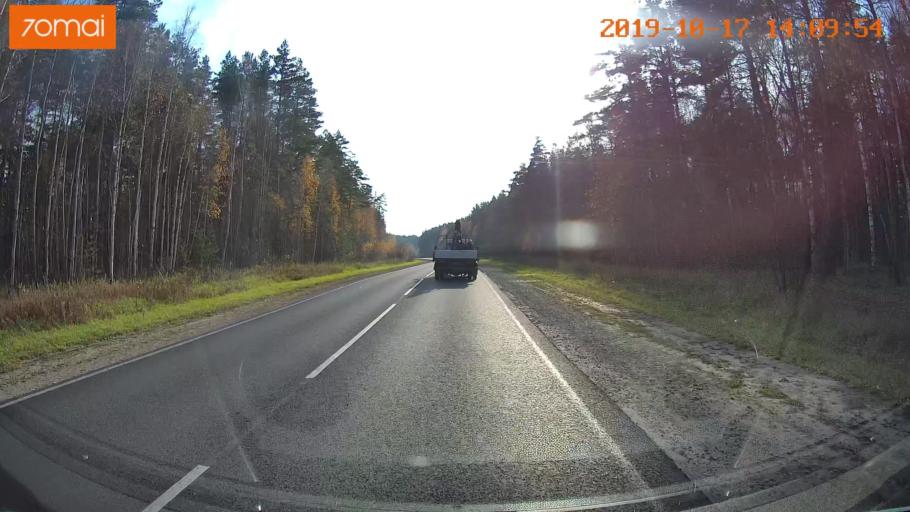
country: RU
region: Rjazan
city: Spas-Klepiki
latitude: 55.0844
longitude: 40.0539
